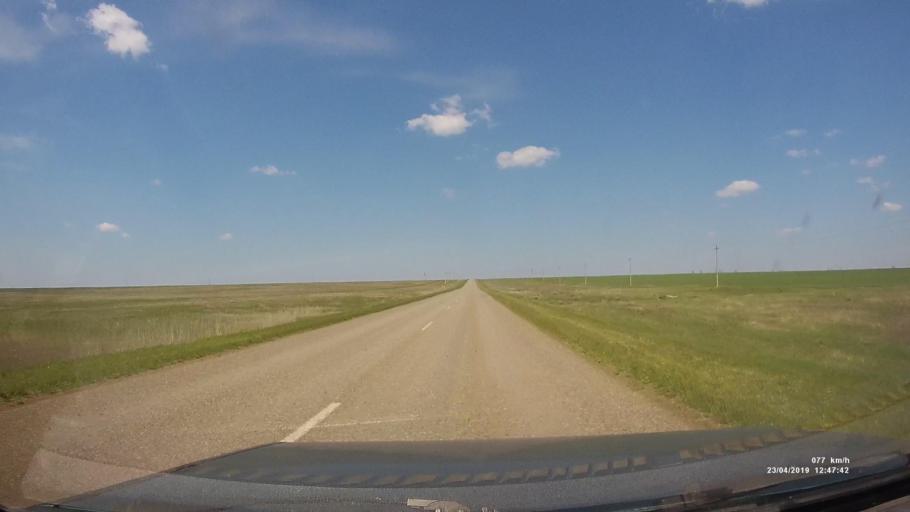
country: RU
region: Kalmykiya
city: Yashalta
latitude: 46.5152
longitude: 42.6387
